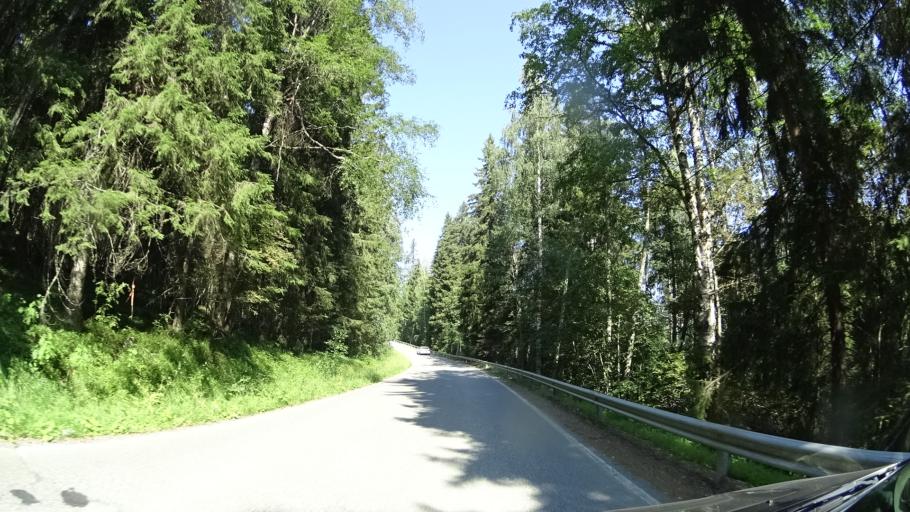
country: FI
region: North Karelia
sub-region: Pielisen Karjala
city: Lieksa
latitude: 63.1137
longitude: 29.8050
